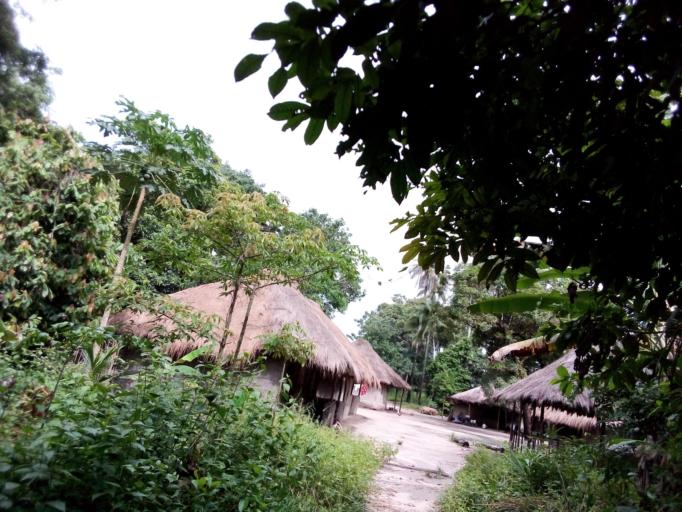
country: SL
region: Southern Province
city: Bonthe
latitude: 7.5105
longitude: -12.5534
